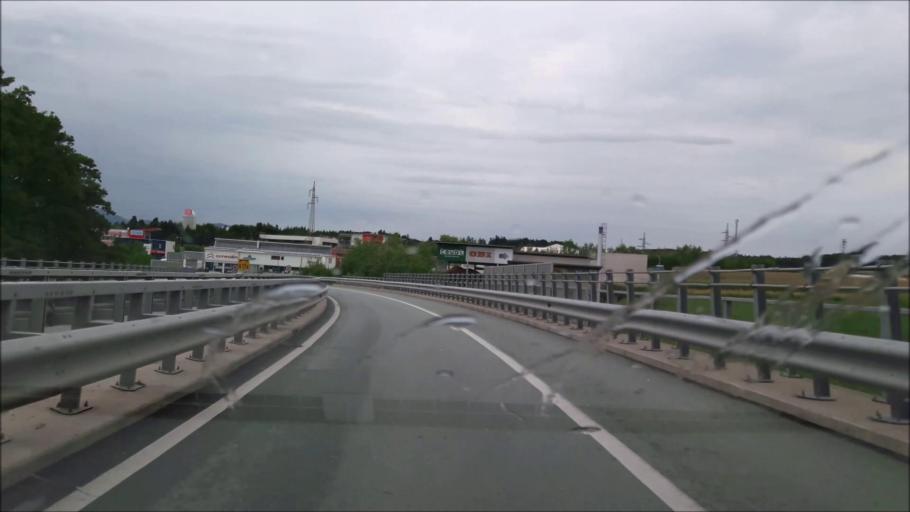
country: AT
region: Styria
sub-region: Politischer Bezirk Hartberg-Fuerstenfeld
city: Sankt Johann in der Haide
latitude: 47.2778
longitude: 16.0105
